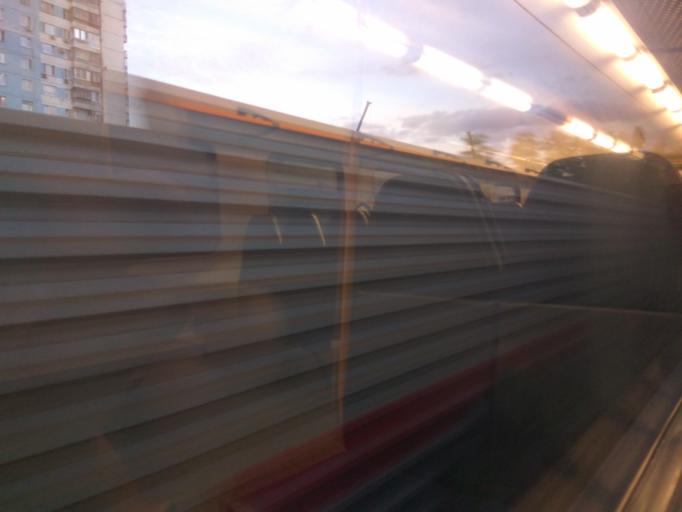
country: RU
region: Moscow
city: Solntsevo
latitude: 55.6494
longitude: 37.3803
